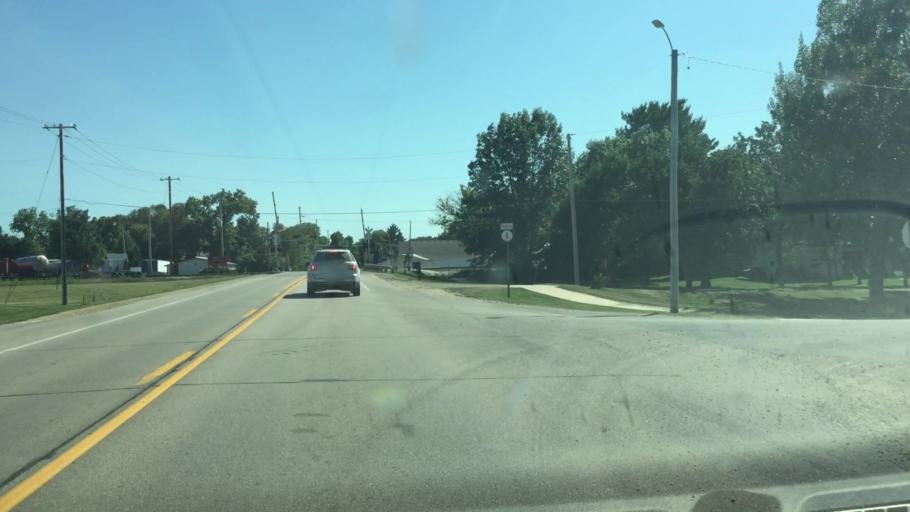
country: US
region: Iowa
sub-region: Linn County
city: Mount Vernon
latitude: 41.9306
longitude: -91.4091
